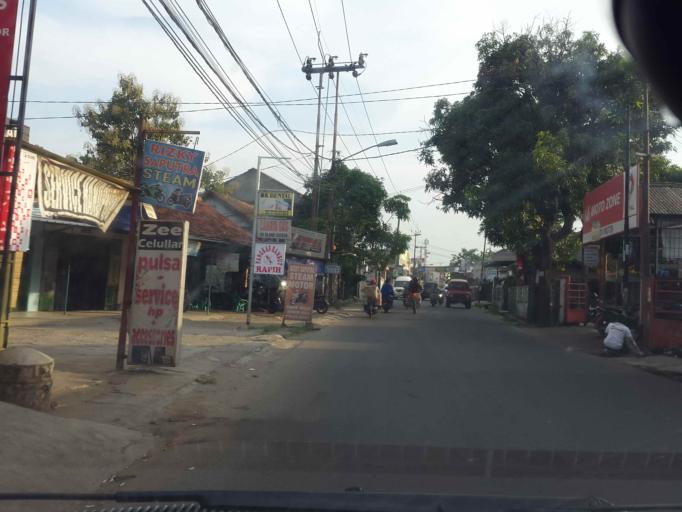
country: ID
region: West Java
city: Ciputat
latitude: -6.2545
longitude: 106.7037
